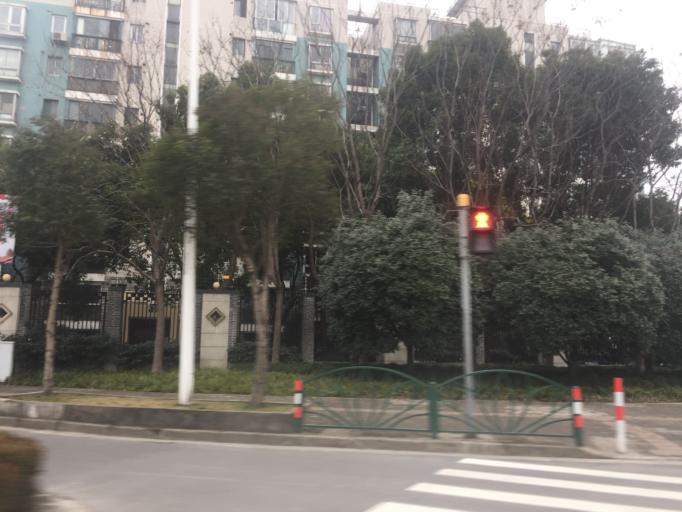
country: CN
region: Shanghai Shi
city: Luwan
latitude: 31.1882
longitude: 121.4961
